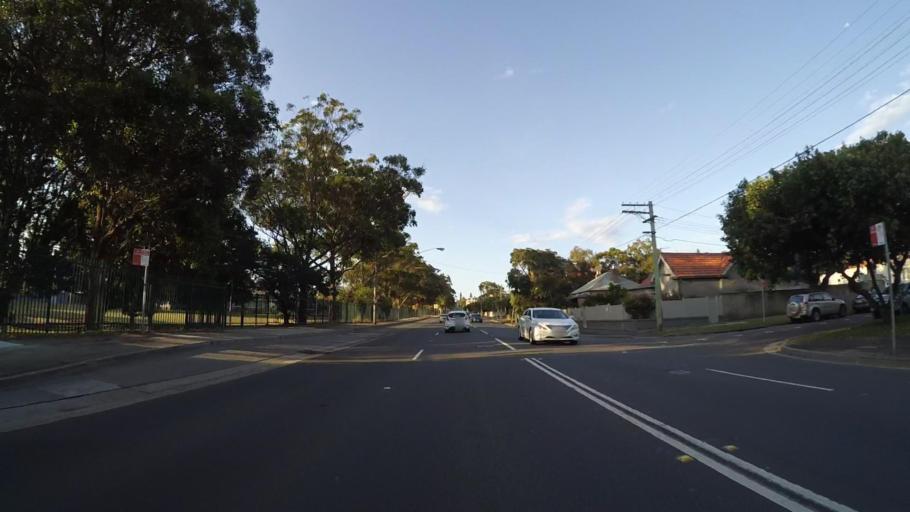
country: AU
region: New South Wales
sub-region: Randwick
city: Daceyville
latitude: -33.9249
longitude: 151.2395
